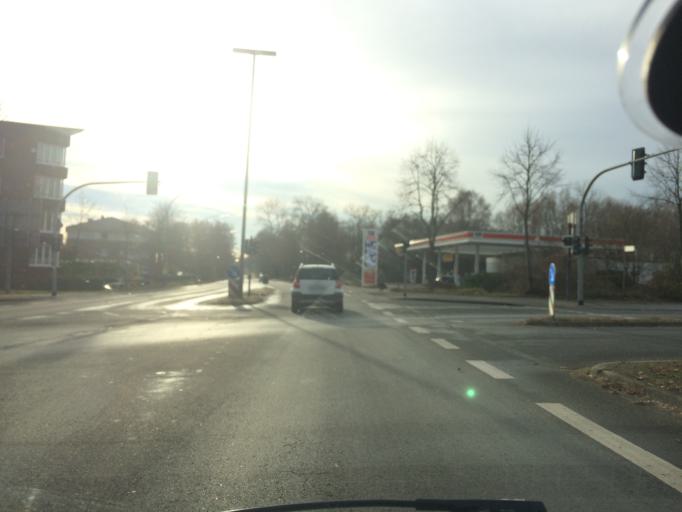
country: DE
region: North Rhine-Westphalia
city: Dorsten
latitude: 51.6564
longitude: 6.9660
